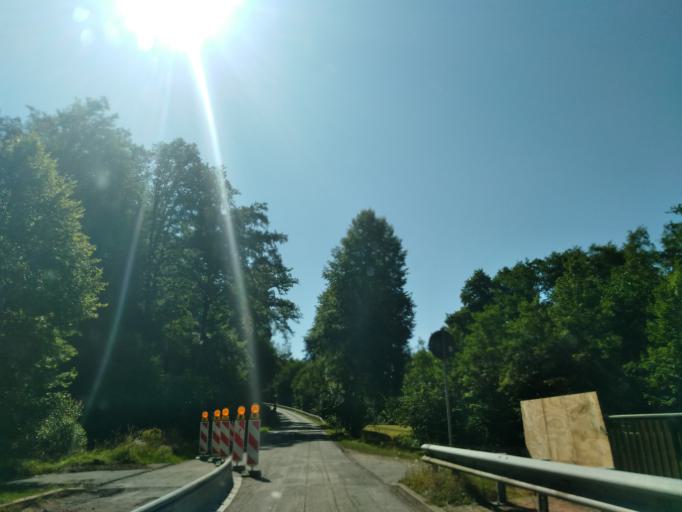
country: DE
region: Baden-Wuerttemberg
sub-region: Karlsruhe Region
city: Buchen
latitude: 49.5480
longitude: 9.2918
